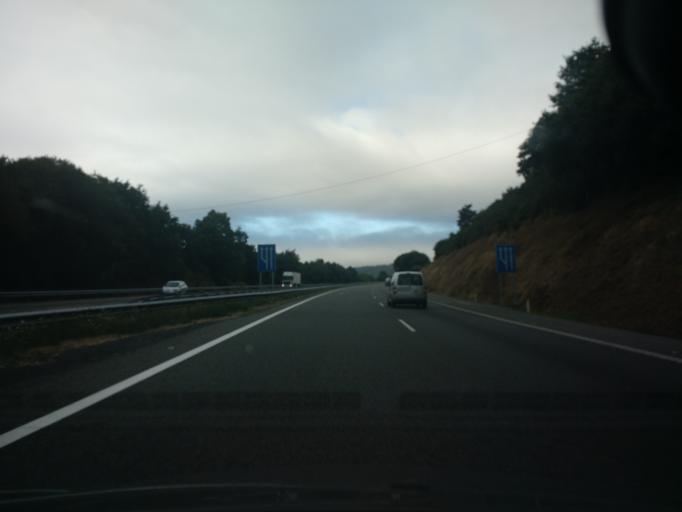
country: ES
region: Galicia
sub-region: Provincia da Coruna
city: Abegondo
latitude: 43.2099
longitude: -8.2804
